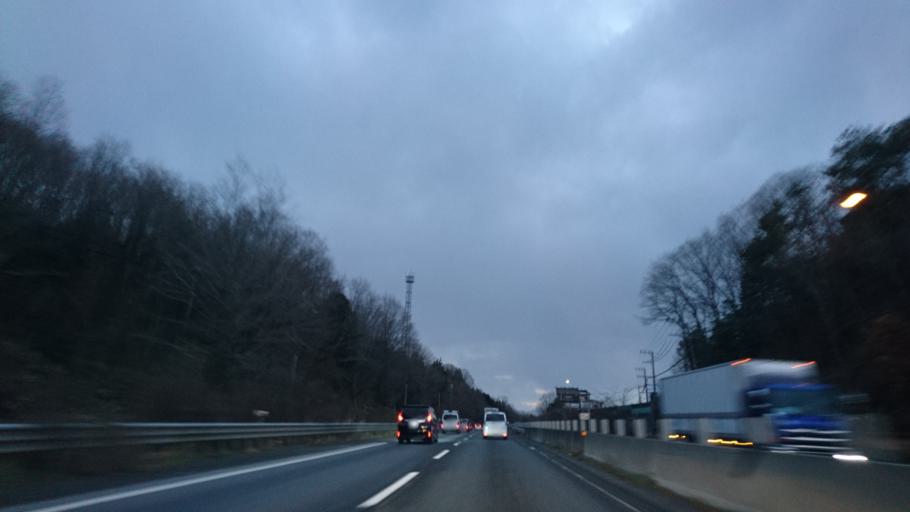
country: JP
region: Nara
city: Haibara-akanedai
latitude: 34.6243
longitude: 135.9838
